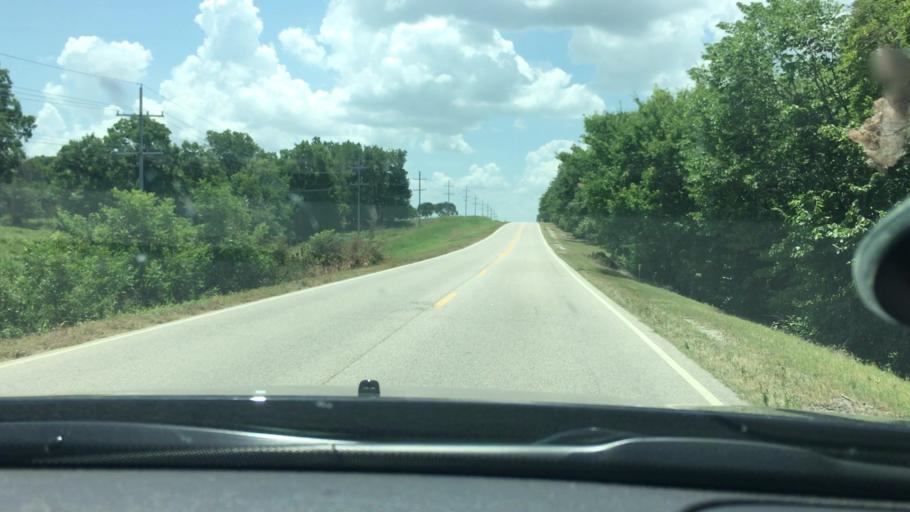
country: US
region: Oklahoma
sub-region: Pontotoc County
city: Ada
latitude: 34.6777
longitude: -96.6349
